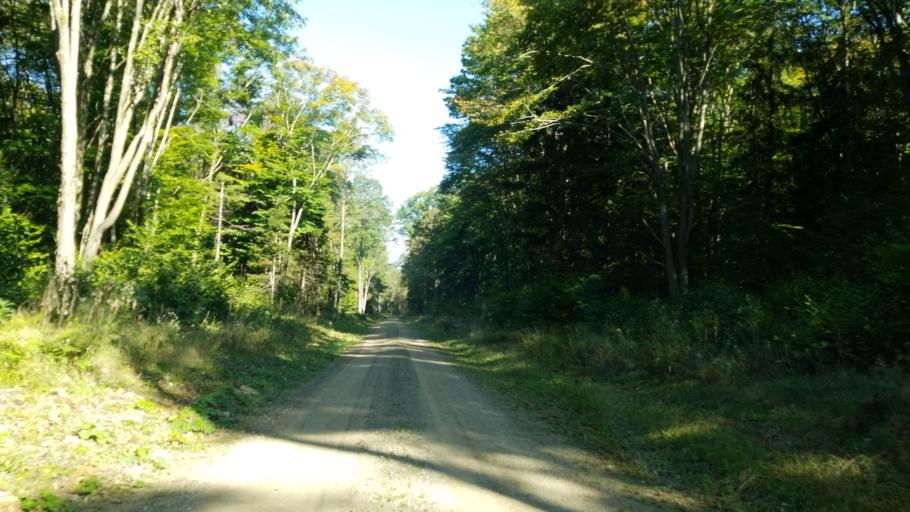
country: US
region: Pennsylvania
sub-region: Clearfield County
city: Curwensville
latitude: 41.1278
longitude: -78.5648
